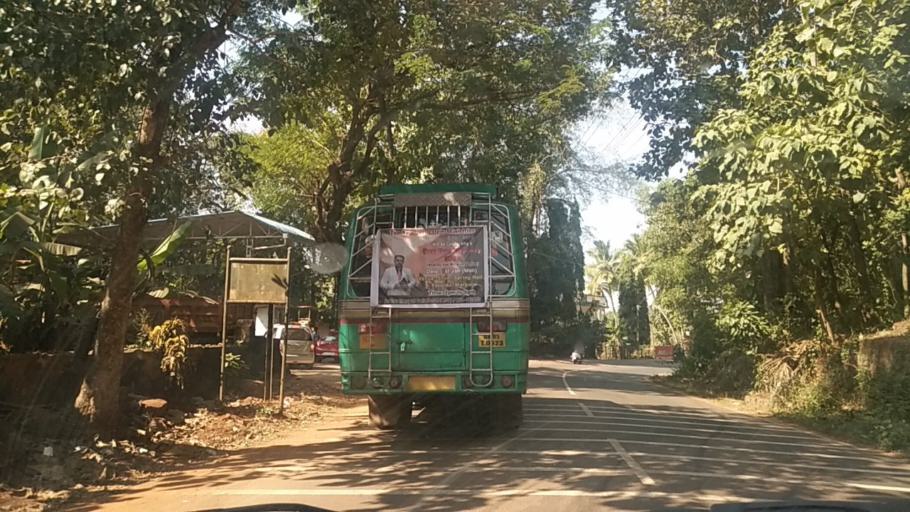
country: IN
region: Goa
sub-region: South Goa
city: Sanguem
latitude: 15.2266
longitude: 74.1395
